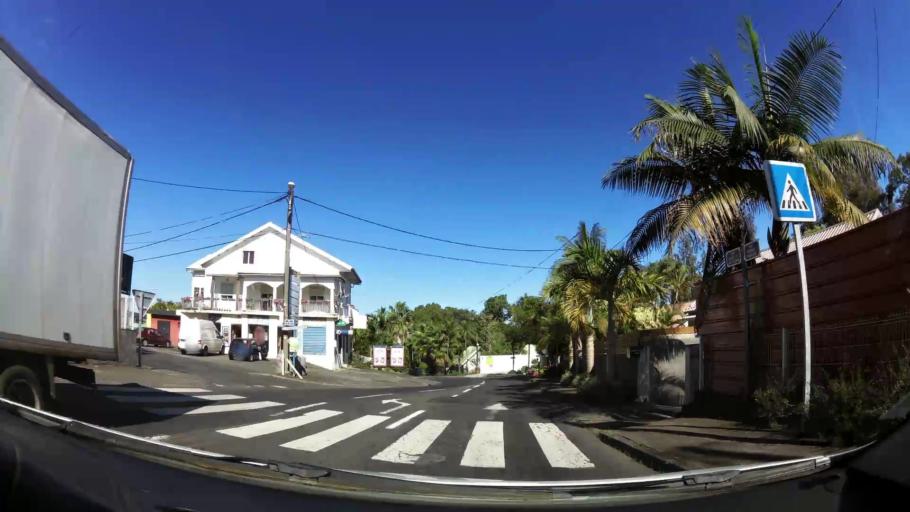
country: RE
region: Reunion
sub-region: Reunion
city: Le Tampon
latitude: -21.2673
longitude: 55.5242
